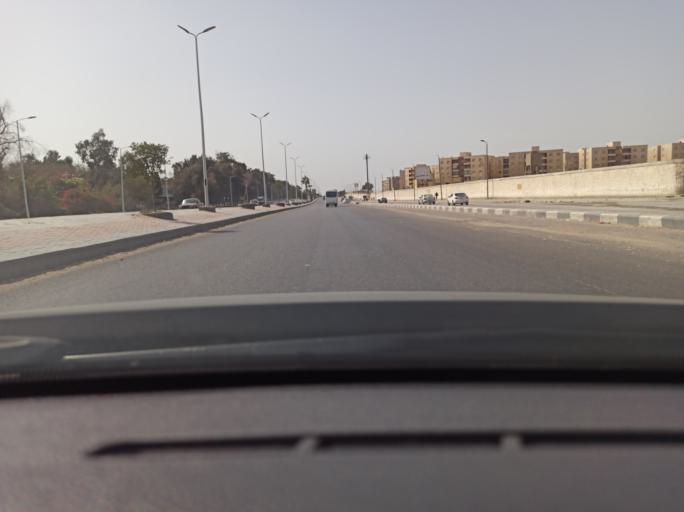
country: EG
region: Muhafazat al Qahirah
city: Halwan
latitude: 29.8305
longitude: 31.3551
